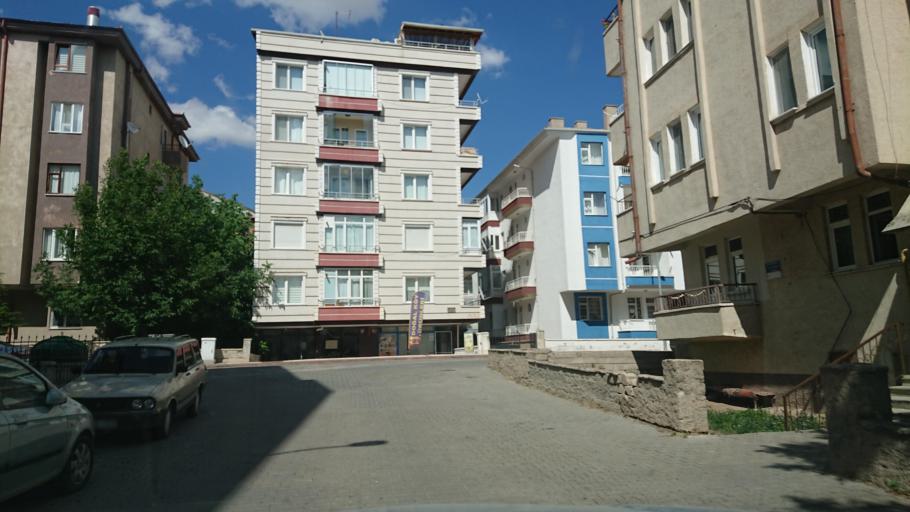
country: TR
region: Kirsehir
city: Kirsehir
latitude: 39.1526
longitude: 34.1572
